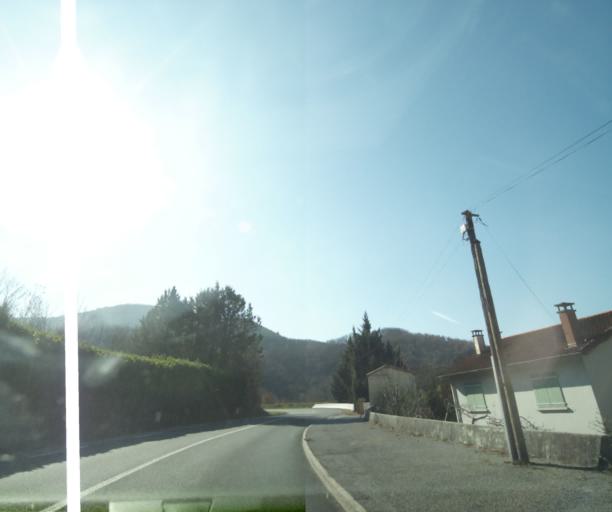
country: FR
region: Midi-Pyrenees
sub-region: Departement de l'Aveyron
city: Saint-Affrique
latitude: 43.9473
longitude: 2.9037
